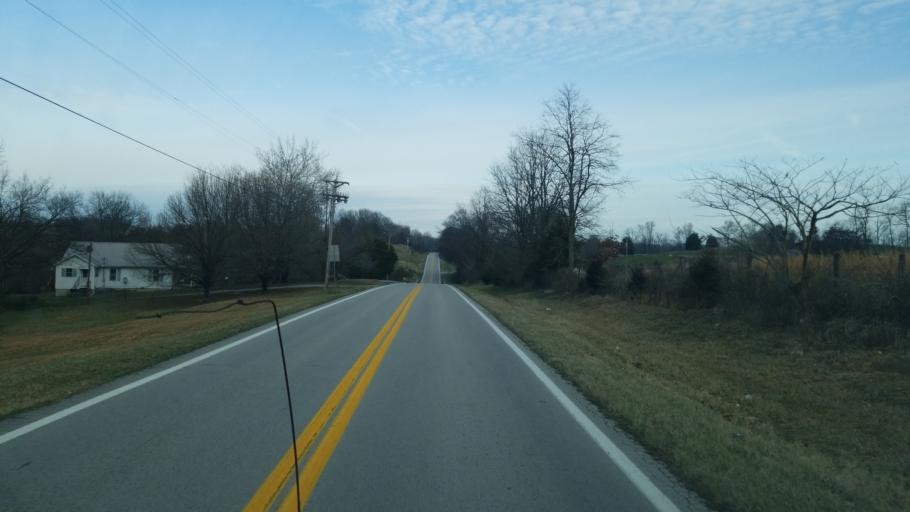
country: US
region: Kentucky
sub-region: Clinton County
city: Albany
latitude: 36.7873
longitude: -85.1784
